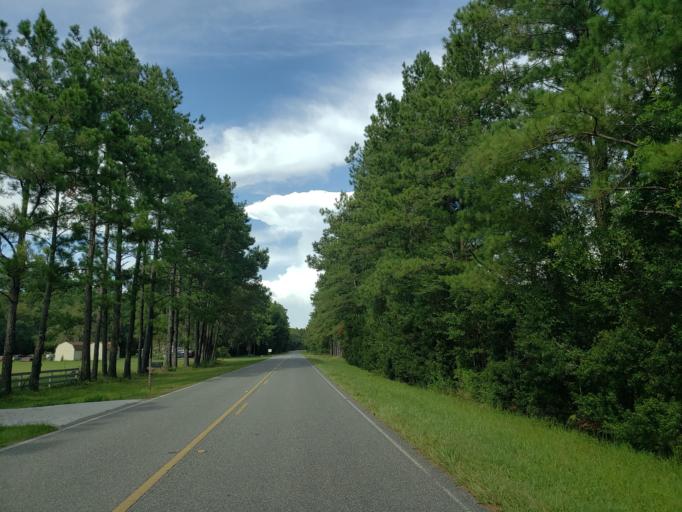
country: US
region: Georgia
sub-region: Echols County
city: Statenville
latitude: 30.6199
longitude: -83.2097
